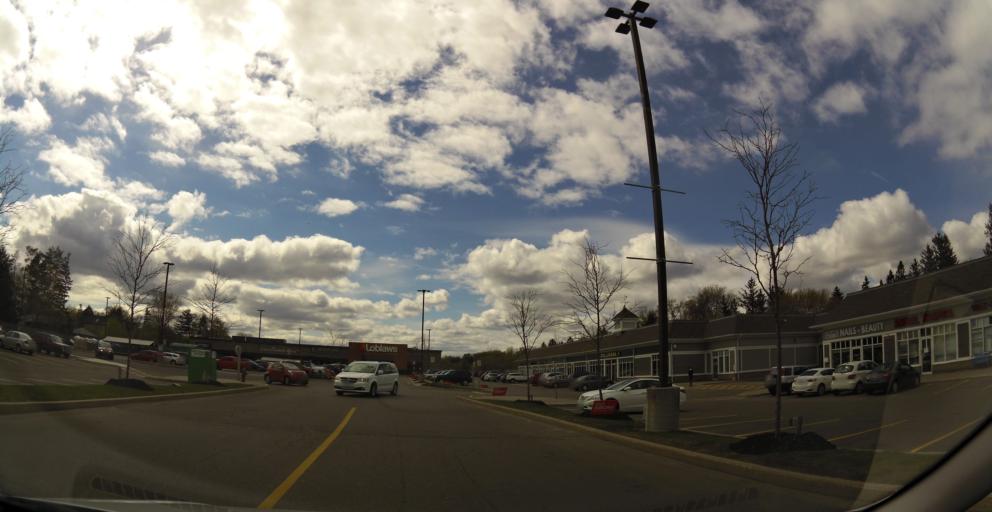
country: CA
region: Ontario
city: Mississauga
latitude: 43.5464
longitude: -79.5921
